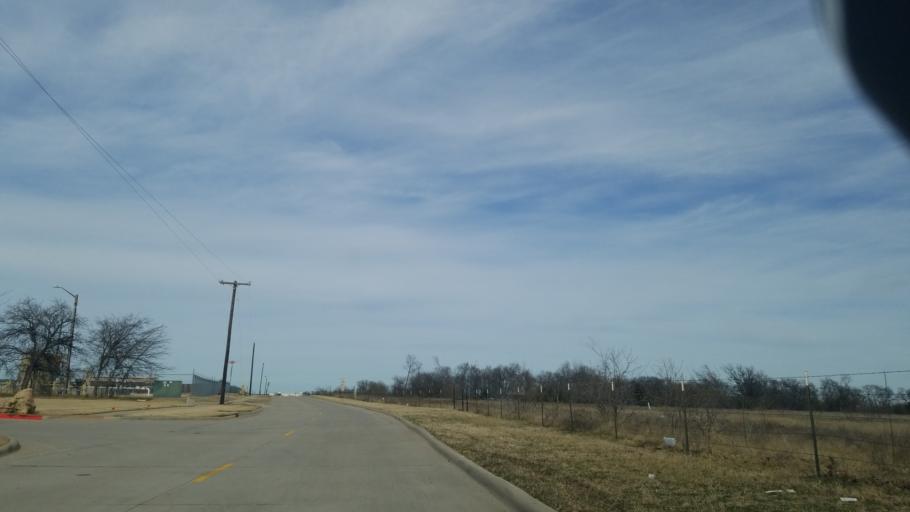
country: US
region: Texas
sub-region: Denton County
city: Denton
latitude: 33.1930
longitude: -97.1906
